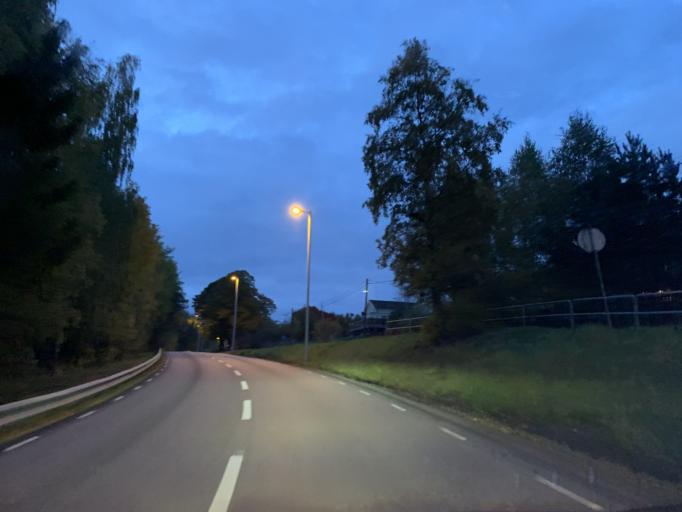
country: SE
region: Stockholm
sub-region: Botkyrka Kommun
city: Varsta
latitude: 59.1669
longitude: 17.7982
